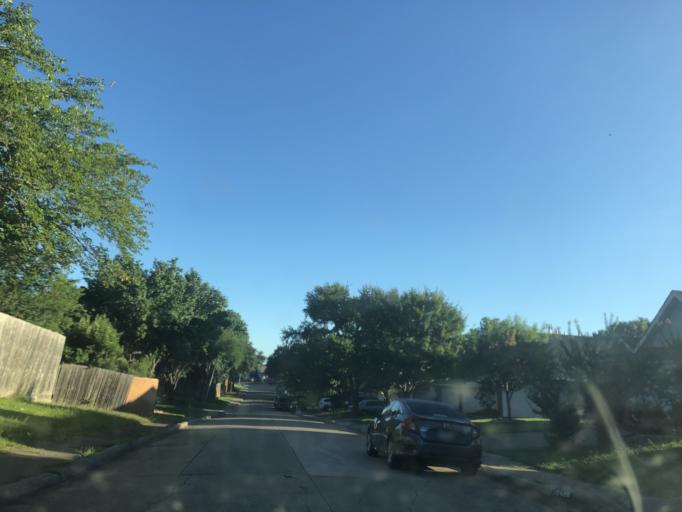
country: US
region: Texas
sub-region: Dallas County
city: Garland
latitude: 32.8386
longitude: -96.6362
